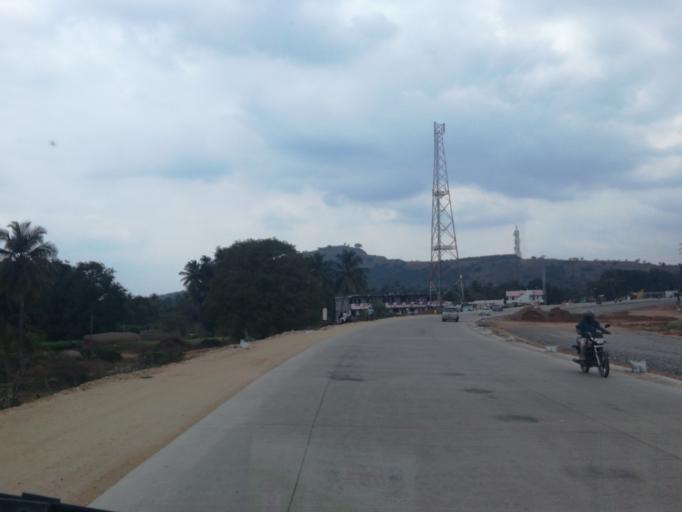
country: IN
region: Andhra Pradesh
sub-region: Chittoor
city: Ramapuram
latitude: 13.0949
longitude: 79.1320
